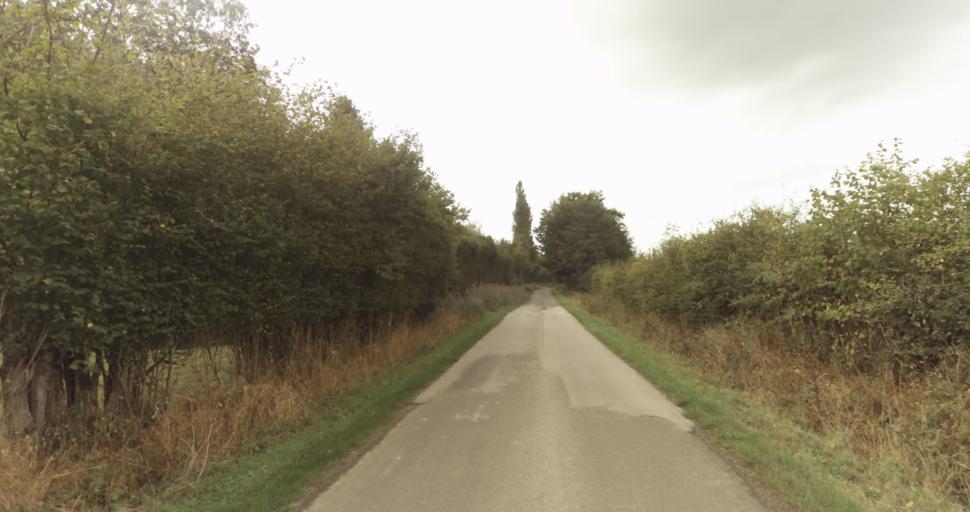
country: FR
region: Lower Normandy
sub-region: Departement de l'Orne
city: Gace
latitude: 48.8205
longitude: 0.3650
